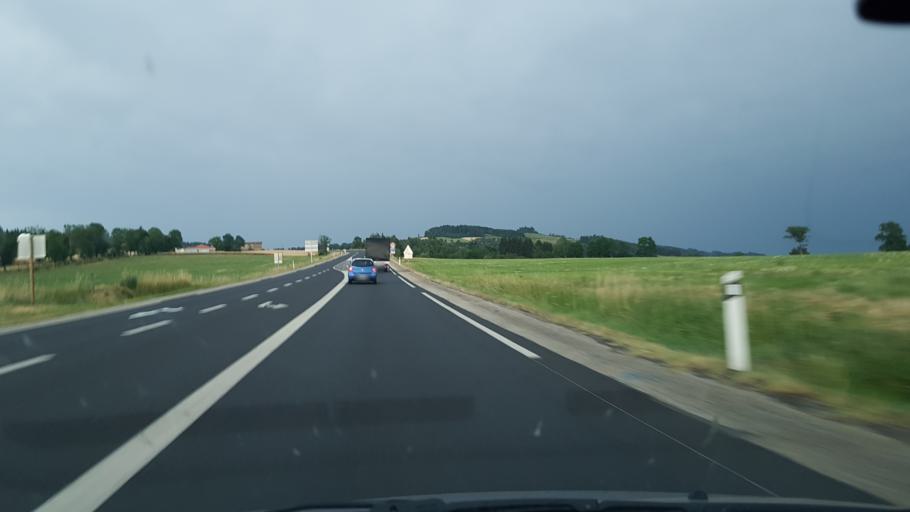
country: FR
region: Auvergne
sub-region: Departement de la Haute-Loire
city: Allegre
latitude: 45.1380
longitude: 3.6321
